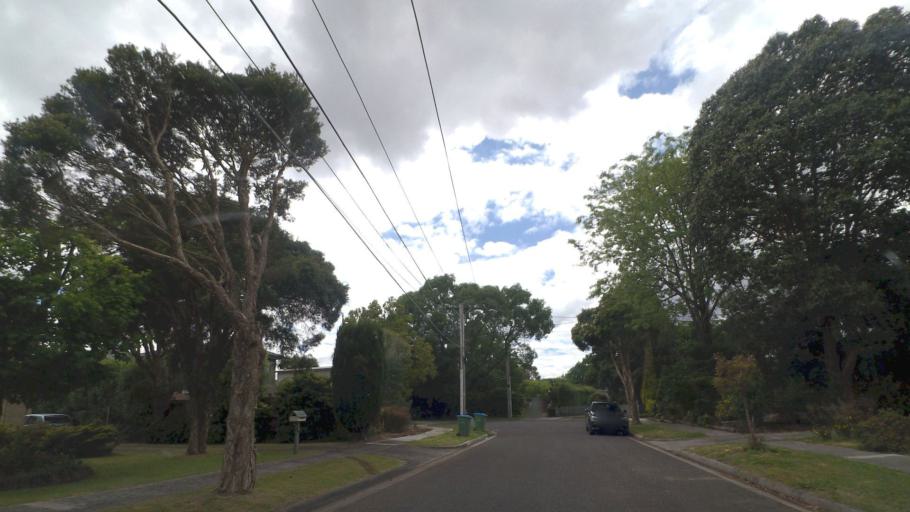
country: AU
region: Victoria
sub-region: Maroondah
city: Croydon North
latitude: -37.8016
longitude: 145.2978
